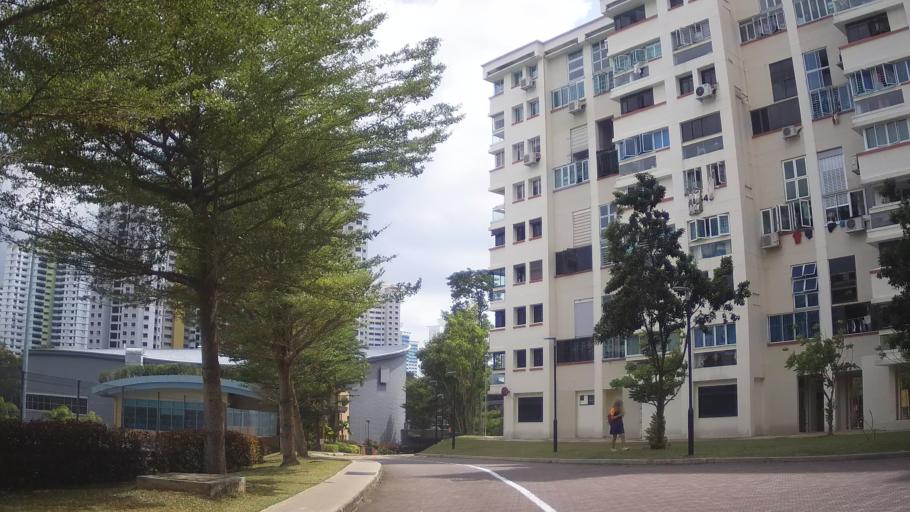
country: MY
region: Johor
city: Johor Bahru
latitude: 1.3828
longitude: 103.7644
